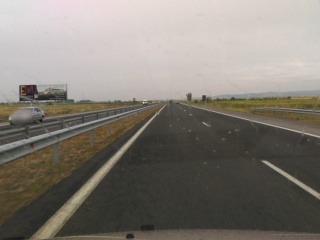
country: BG
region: Sliven
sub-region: Obshtina Nova Zagora
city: Nova Zagora
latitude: 42.4159
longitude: 25.9353
